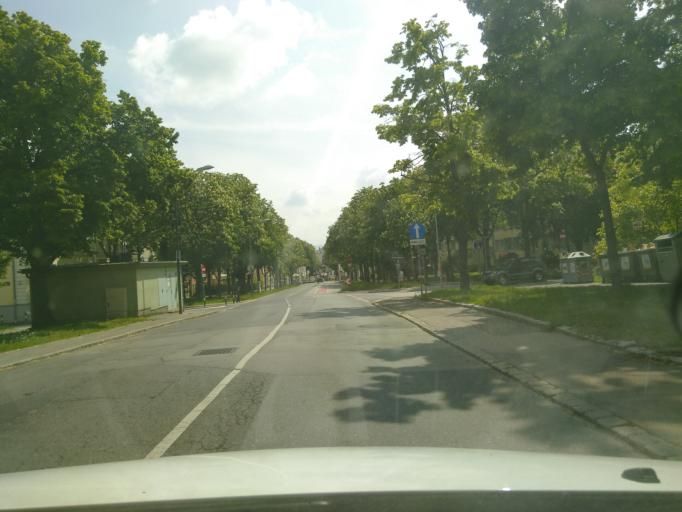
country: AT
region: Lower Austria
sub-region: Politischer Bezirk Modling
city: Vosendorf
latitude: 48.1689
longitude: 16.3100
